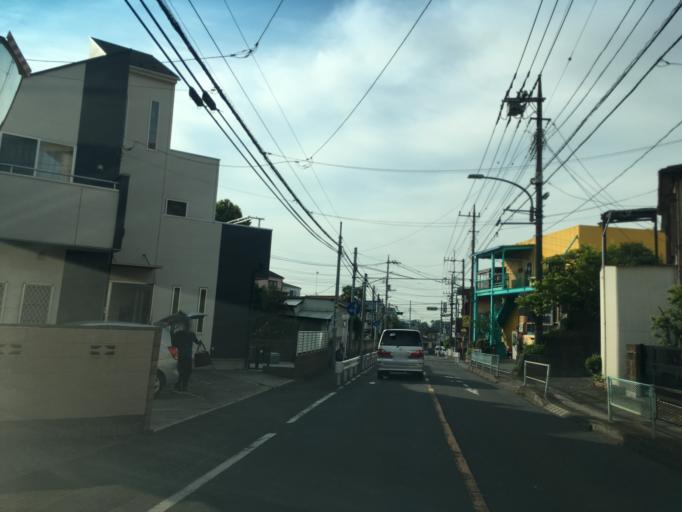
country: JP
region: Saitama
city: Tokorozawa
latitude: 35.7886
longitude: 139.5064
